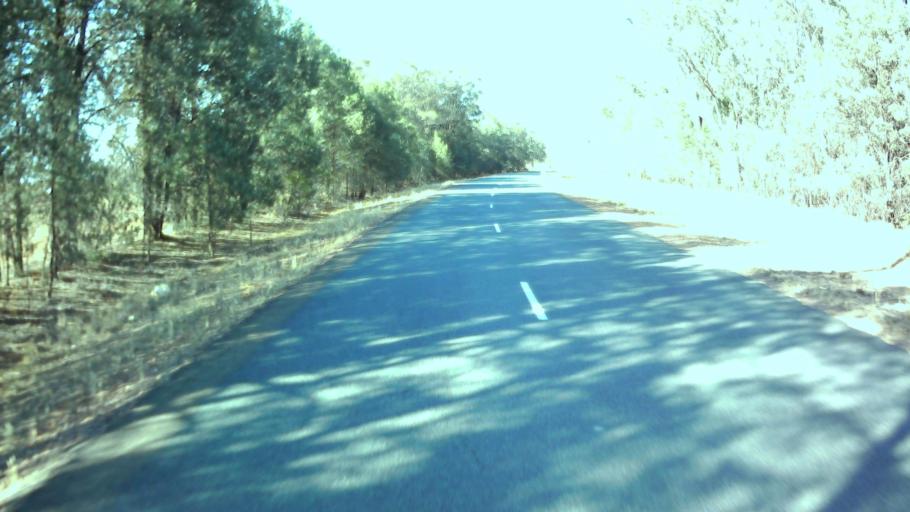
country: AU
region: New South Wales
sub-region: Weddin
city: Grenfell
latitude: -34.0326
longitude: 148.0911
